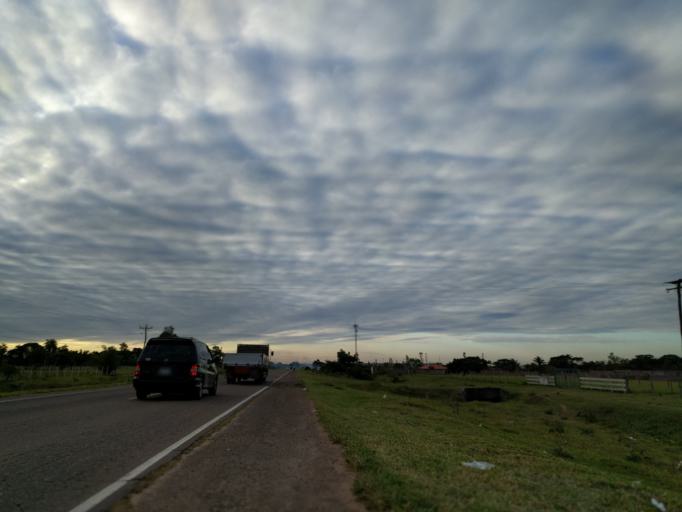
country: BO
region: Santa Cruz
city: Santa Rita
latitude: -17.8882
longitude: -63.2638
